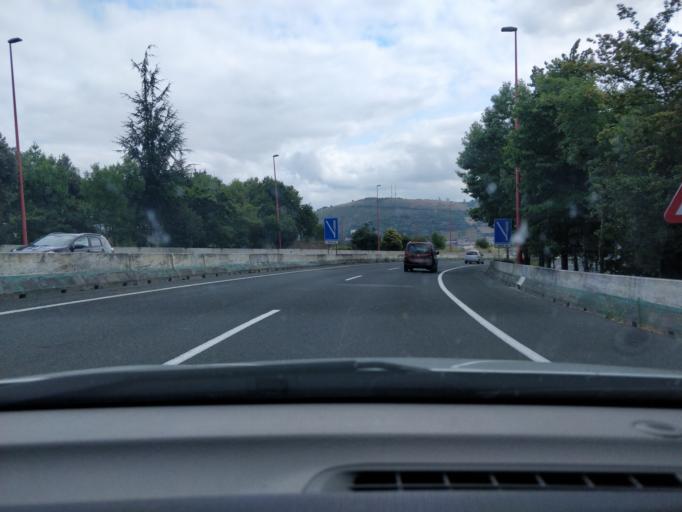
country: ES
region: Basque Country
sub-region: Bizkaia
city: Alonsotegi
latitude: 43.2707
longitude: -2.9699
